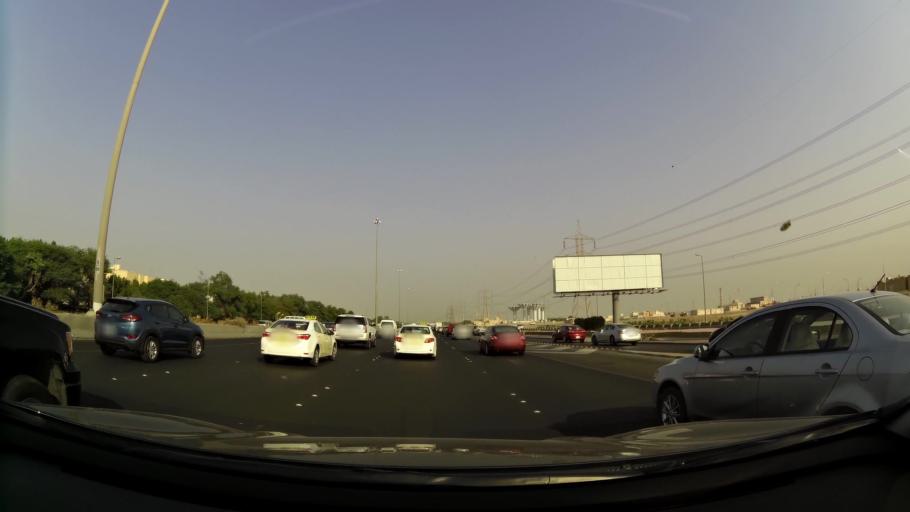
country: KW
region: Al Farwaniyah
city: Janub as Surrah
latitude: 29.3043
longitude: 47.9853
